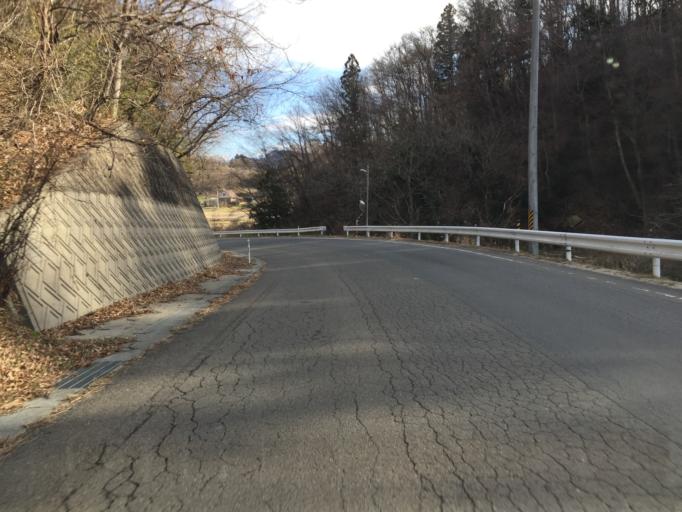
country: JP
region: Fukushima
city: Fukushima-shi
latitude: 37.6895
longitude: 140.5547
